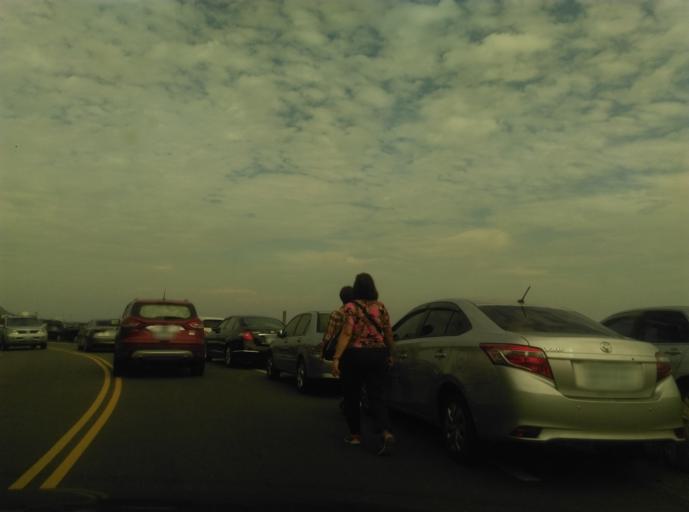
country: TW
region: Taiwan
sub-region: Keelung
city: Keelung
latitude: 25.1925
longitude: 121.6852
